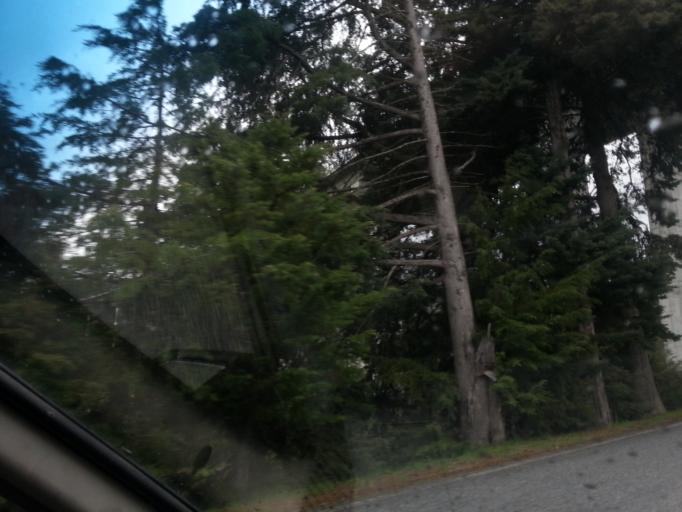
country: PT
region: Guarda
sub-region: Fornos de Algodres
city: Fornos de Algodres
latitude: 40.6239
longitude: -7.5881
